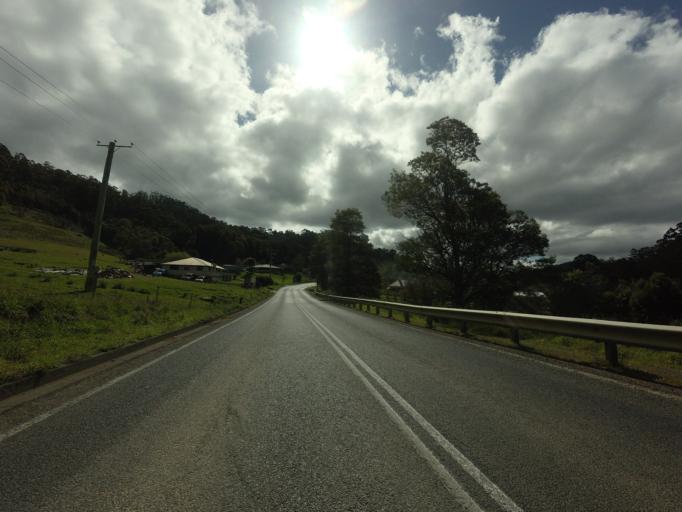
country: AU
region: Tasmania
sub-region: Huon Valley
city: Geeveston
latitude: -43.3044
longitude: 147.0081
